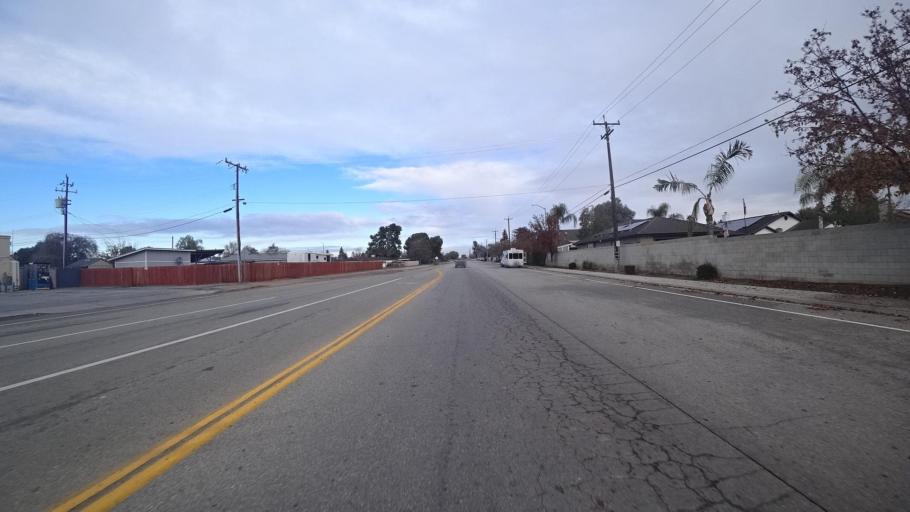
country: US
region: California
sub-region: Kern County
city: Greenacres
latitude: 35.4201
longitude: -119.0745
